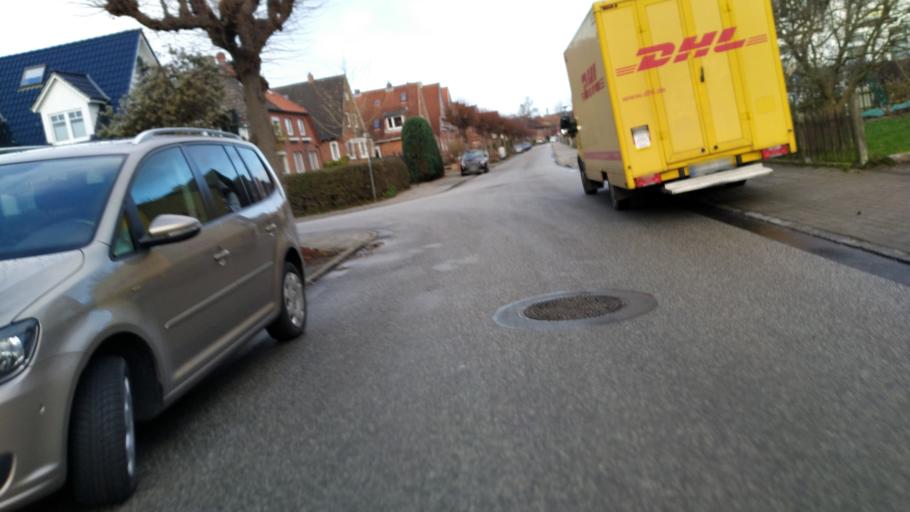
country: DE
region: Schleswig-Holstein
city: Travemuende
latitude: 53.9616
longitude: 10.8710
